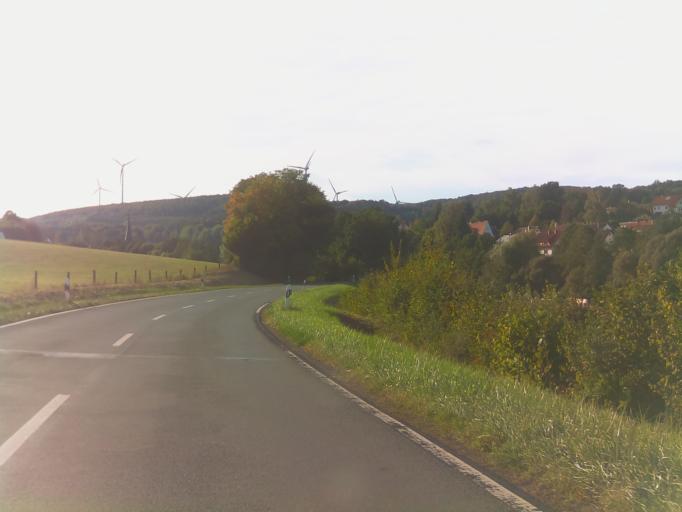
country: DE
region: Hesse
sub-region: Regierungsbezirk Kassel
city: Flieden
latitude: 50.4246
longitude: 9.5233
